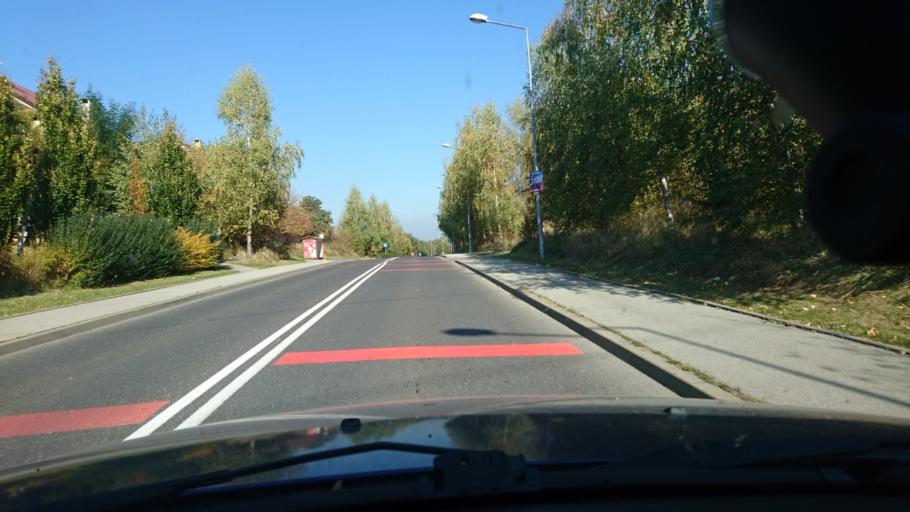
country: PL
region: Silesian Voivodeship
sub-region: Bielsko-Biala
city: Bielsko-Biala
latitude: 49.8337
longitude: 19.0295
